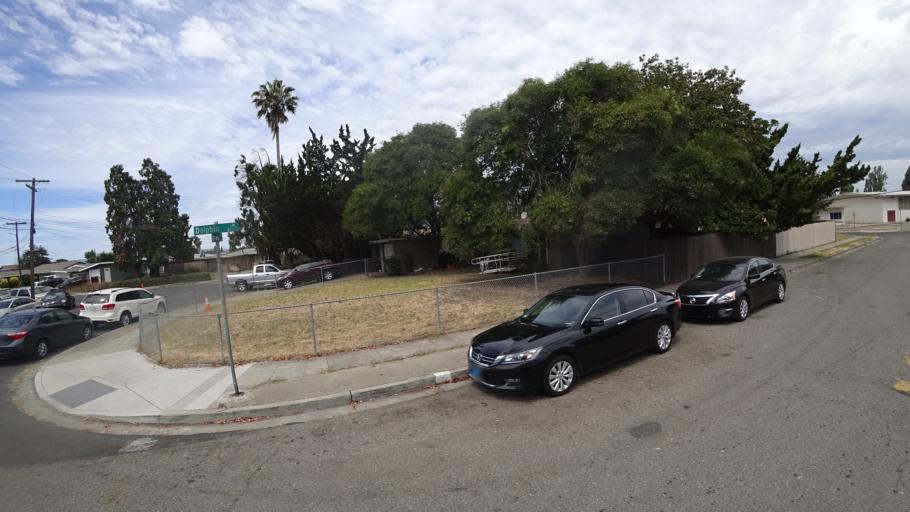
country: US
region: California
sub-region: Alameda County
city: Hayward
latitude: 37.6261
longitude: -122.0854
